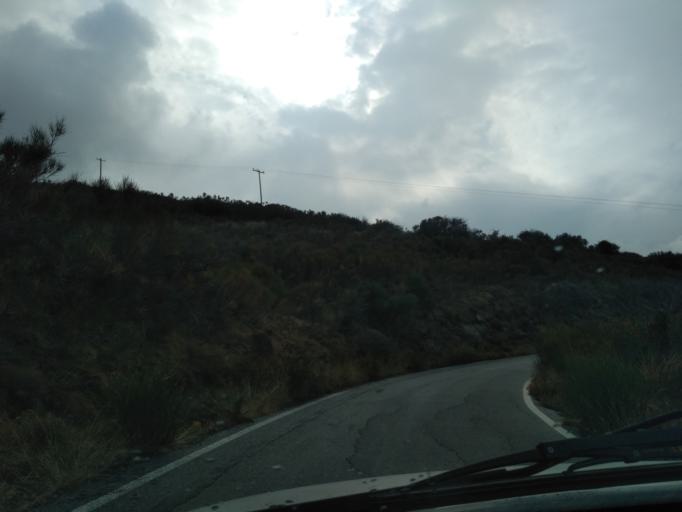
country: GR
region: Crete
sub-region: Nomos Lasithiou
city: Siteia
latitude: 35.1550
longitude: 26.0180
